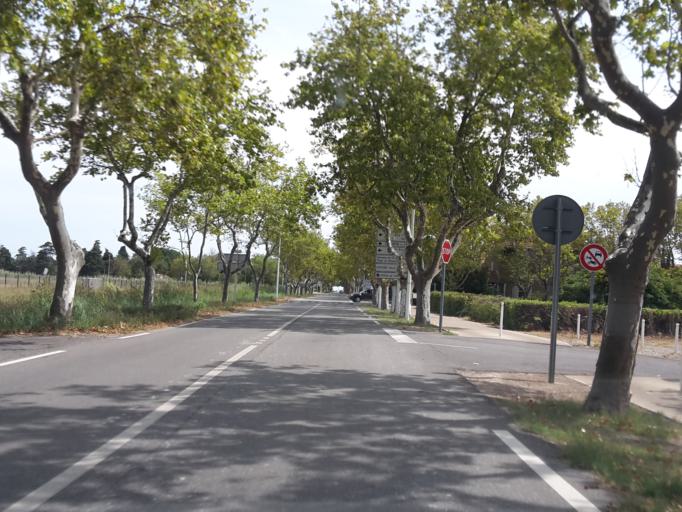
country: FR
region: Provence-Alpes-Cote d'Azur
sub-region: Departement des Bouches-du-Rhone
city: Port-Saint-Louis-du-Rhone
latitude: 43.4176
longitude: 4.7358
